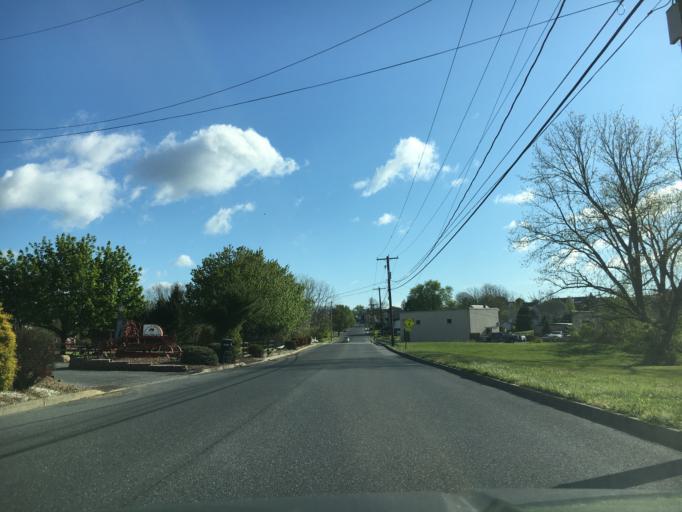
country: US
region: Pennsylvania
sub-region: Lehigh County
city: Stiles
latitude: 40.6665
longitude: -75.5110
